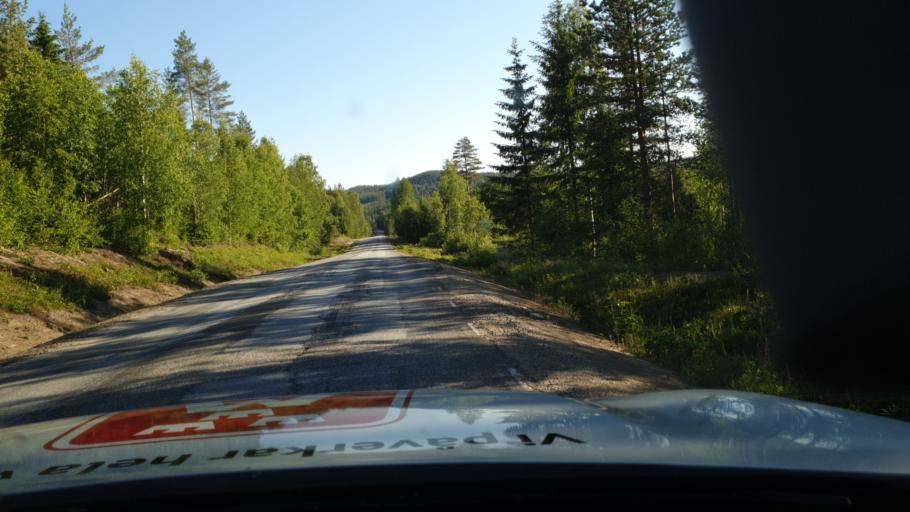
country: SE
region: Vaesterbotten
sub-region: Vannas Kommun
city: Vannasby
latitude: 64.0628
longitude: 20.0638
